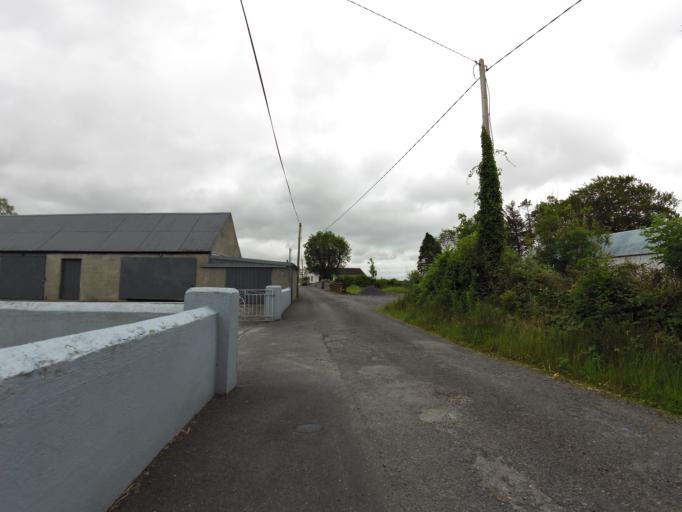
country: IE
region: Connaught
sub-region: County Galway
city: Athenry
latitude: 53.3184
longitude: -8.7189
